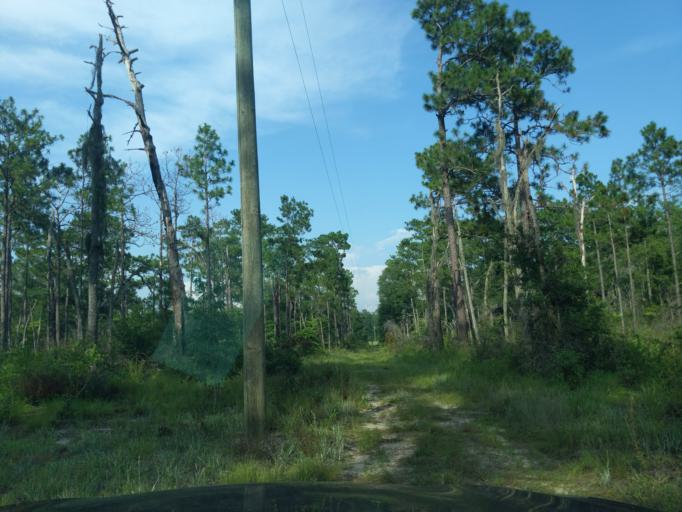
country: US
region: Florida
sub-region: Gadsden County
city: Midway
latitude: 30.4072
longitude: -84.3986
